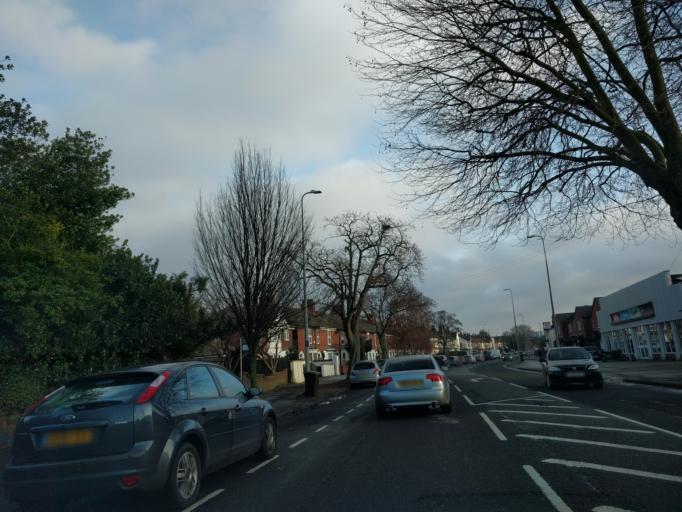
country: GB
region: England
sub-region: Lincolnshire
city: Lincoln
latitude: 53.2333
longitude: -0.5569
